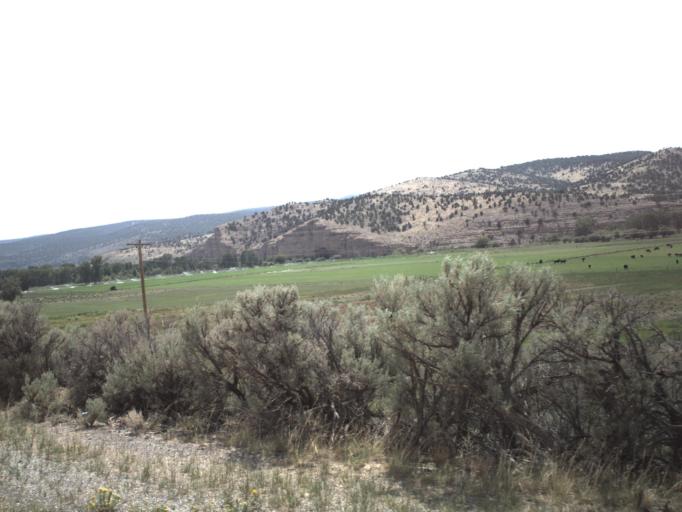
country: US
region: Utah
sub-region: Piute County
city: Junction
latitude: 38.1026
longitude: -111.9849
